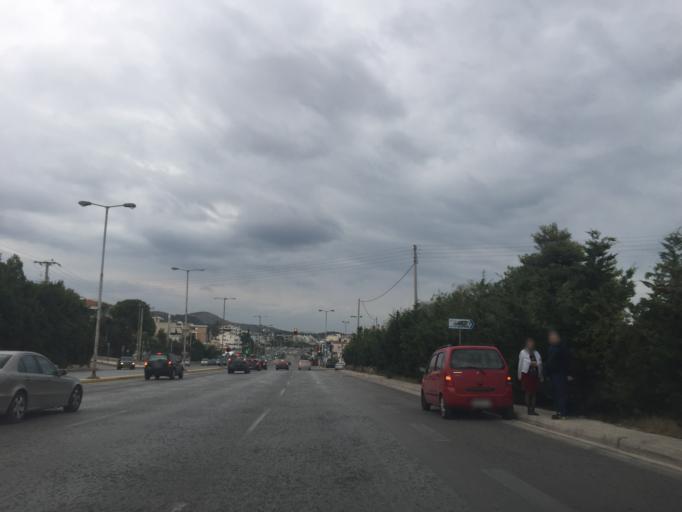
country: GR
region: Attica
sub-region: Nomarchia Anatolikis Attikis
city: Voula
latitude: 37.8459
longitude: 23.7698
